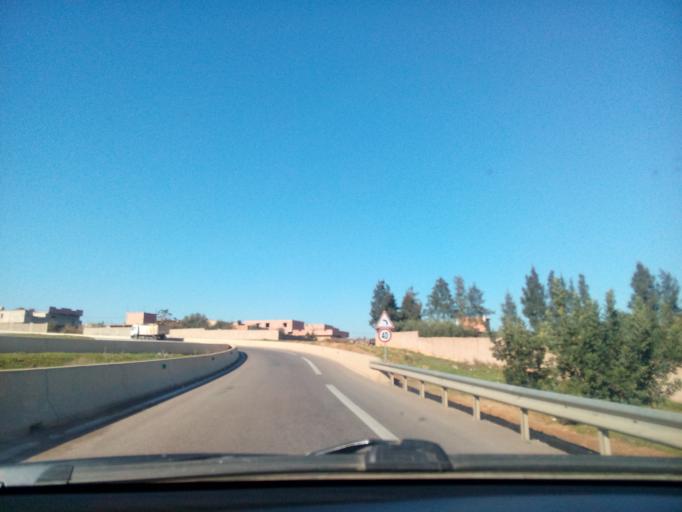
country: DZ
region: Chlef
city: Boukadir
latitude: 36.0555
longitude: 1.1379
